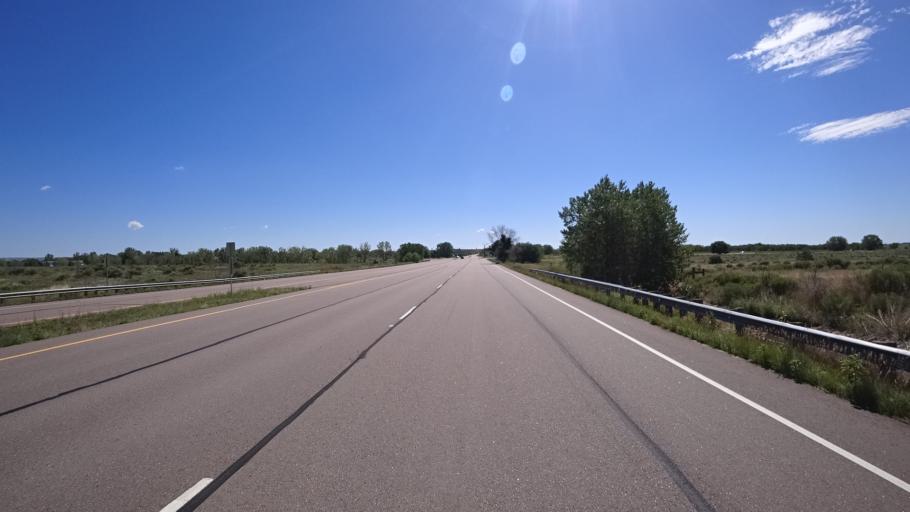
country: US
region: Colorado
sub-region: El Paso County
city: Security-Widefield
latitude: 38.7621
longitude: -104.6627
